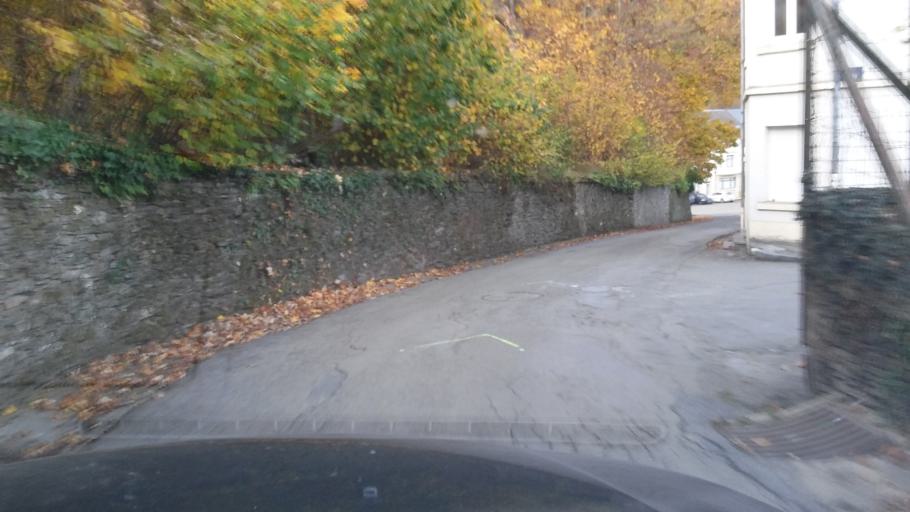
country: BE
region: Wallonia
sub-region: Province du Luxembourg
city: Bouillon
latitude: 49.7961
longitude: 5.0667
